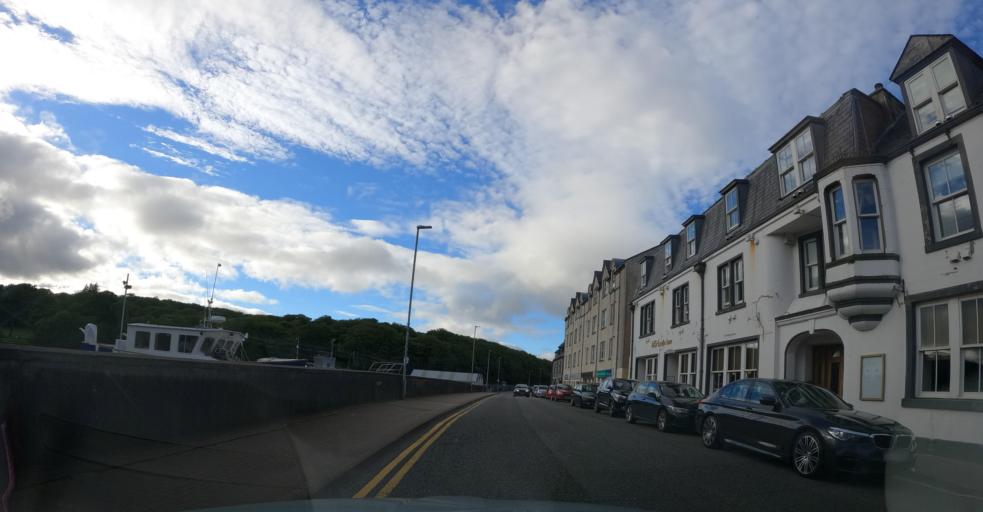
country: GB
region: Scotland
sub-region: Eilean Siar
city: Stornoway
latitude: 58.2105
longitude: -6.3887
